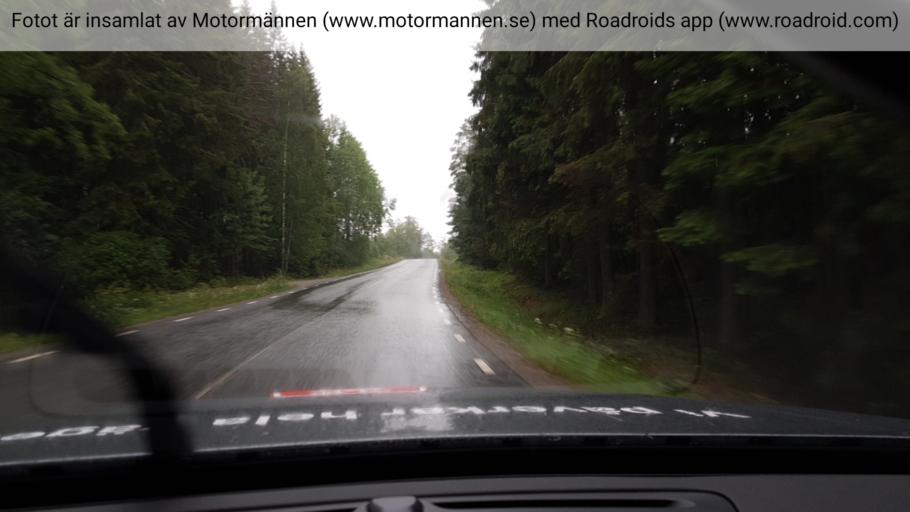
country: SE
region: Vaestmanland
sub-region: Norbergs Kommun
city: Norberg
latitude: 59.9900
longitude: 16.0611
